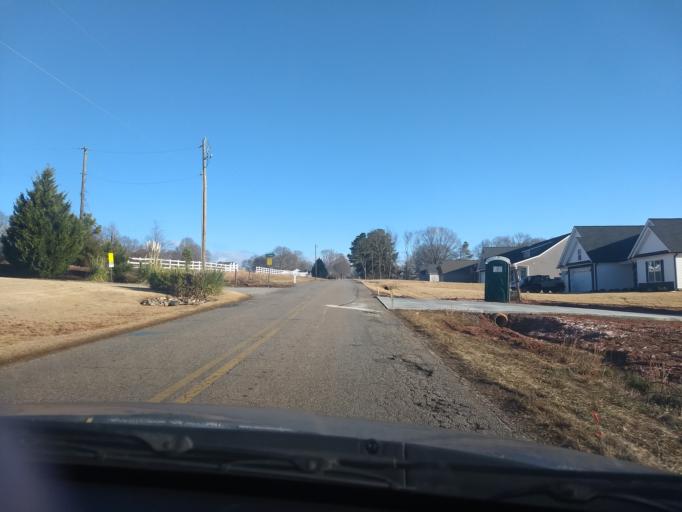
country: US
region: South Carolina
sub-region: Greenville County
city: Greer
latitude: 35.0185
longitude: -82.2050
